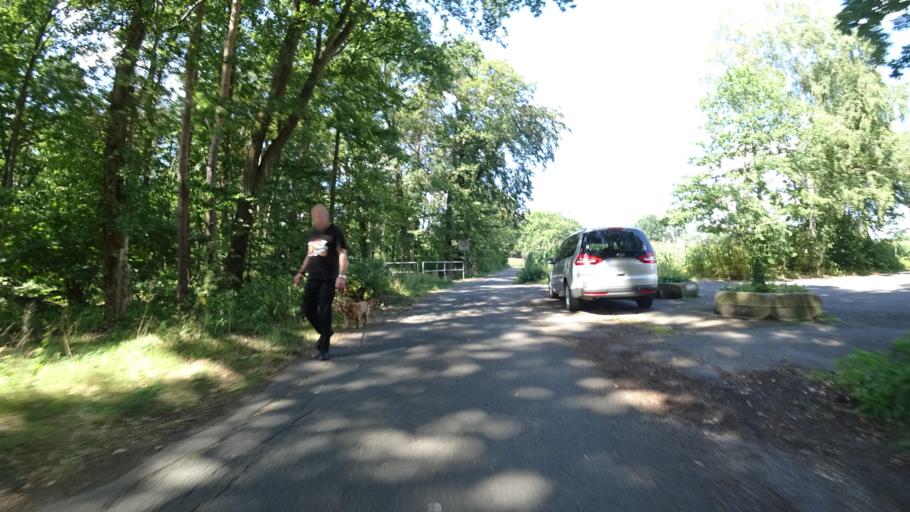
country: DE
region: North Rhine-Westphalia
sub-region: Regierungsbezirk Detmold
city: Guetersloh
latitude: 51.9277
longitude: 8.3961
